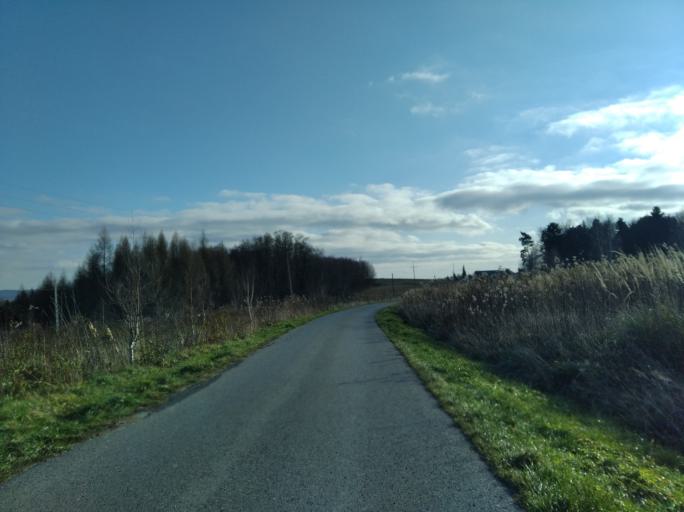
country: PL
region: Subcarpathian Voivodeship
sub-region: Powiat strzyzowski
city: Babica
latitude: 49.9128
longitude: 21.8472
